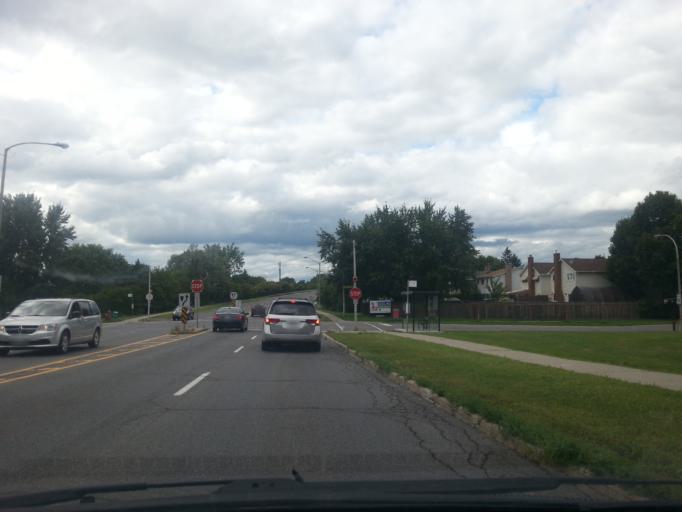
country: CA
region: Quebec
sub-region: Outaouais
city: Gatineau
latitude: 45.4706
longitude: -75.5320
